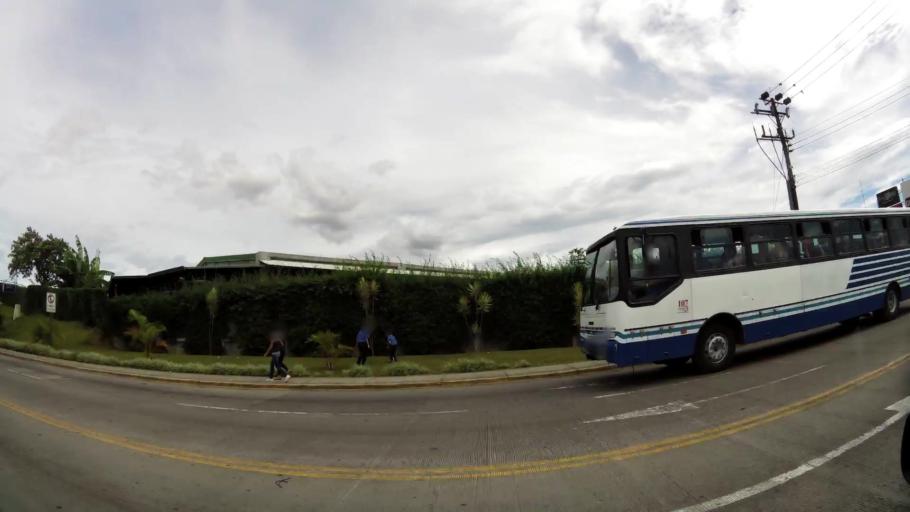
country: CR
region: San Jose
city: Curridabat
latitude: 9.9063
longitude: -84.0497
